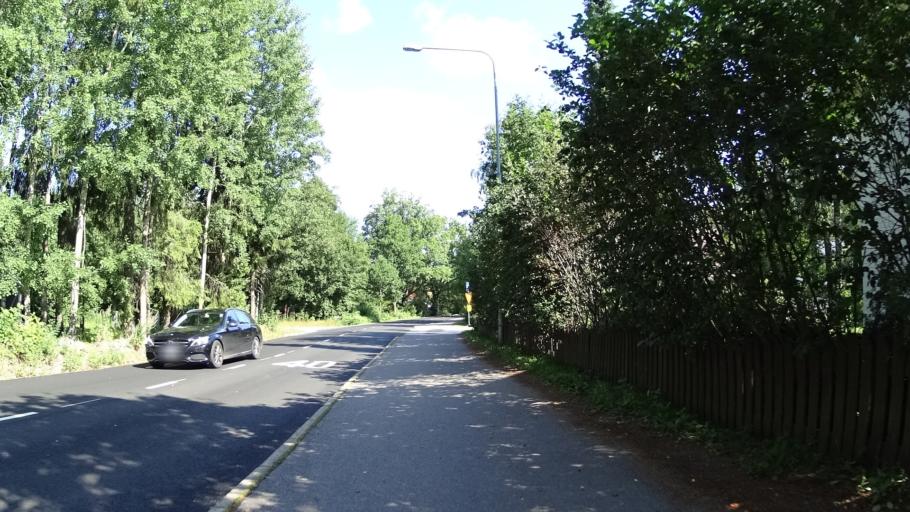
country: FI
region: Uusimaa
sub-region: Helsinki
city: Tuusula
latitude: 60.4096
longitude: 25.0298
